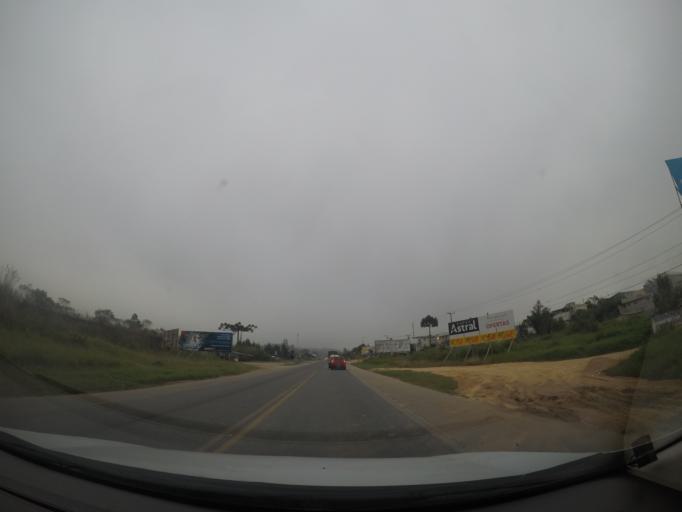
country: BR
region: Parana
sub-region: Almirante Tamandare
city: Almirante Tamandare
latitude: -25.3208
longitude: -49.2995
